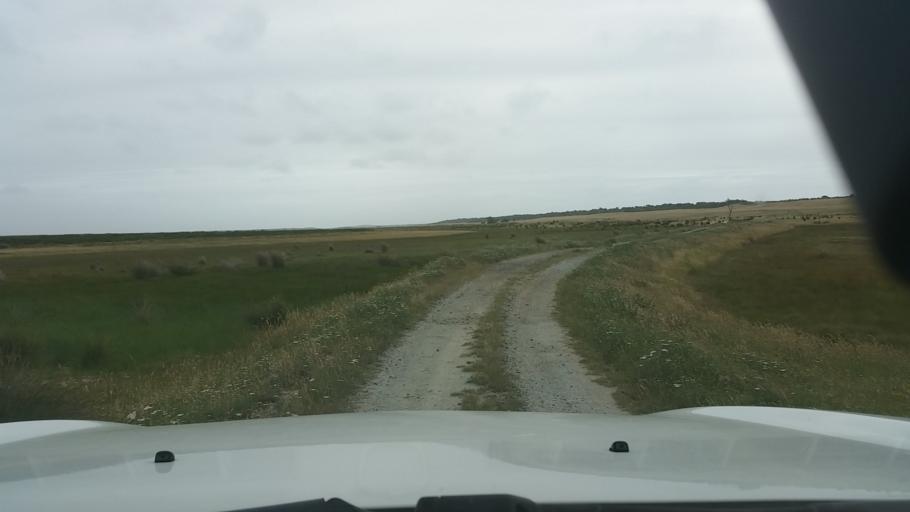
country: NZ
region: Chatham Islands
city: Waitangi
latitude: -43.7949
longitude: -176.3520
